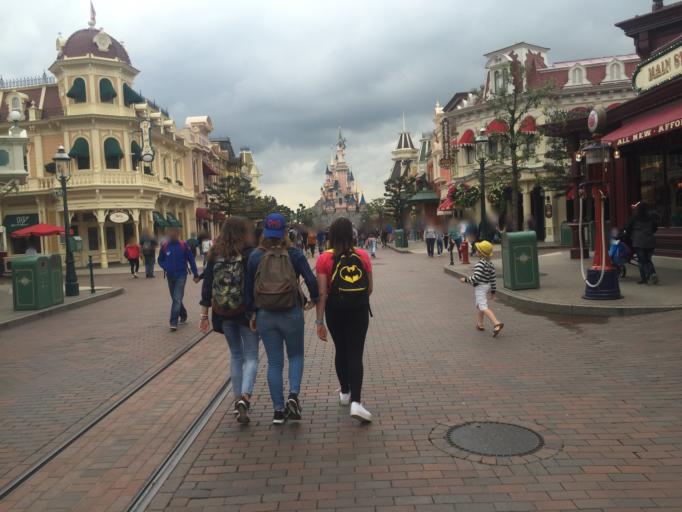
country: FR
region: Ile-de-France
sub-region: Departement de Seine-et-Marne
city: Chessy
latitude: 48.8715
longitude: 2.7782
